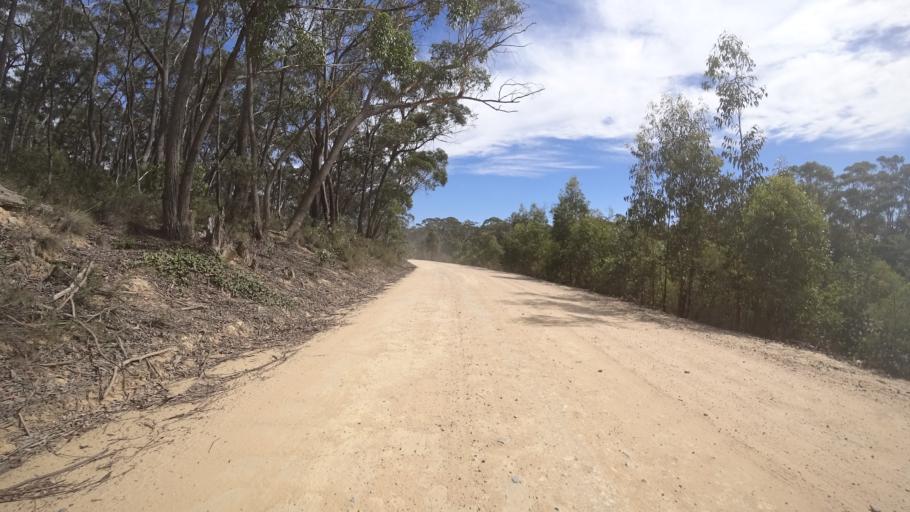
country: AU
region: New South Wales
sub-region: Lithgow
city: Lithgow
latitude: -33.3169
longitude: 150.2460
